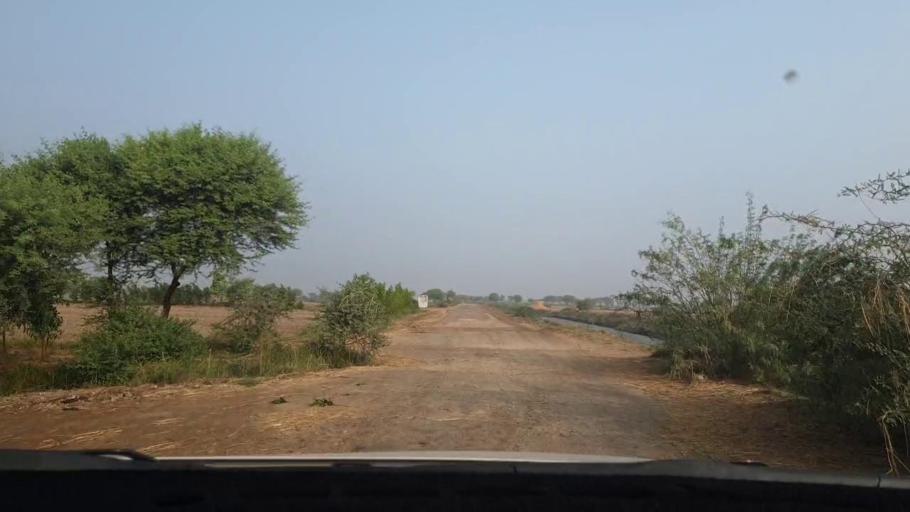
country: PK
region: Sindh
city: Tando Muhammad Khan
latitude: 25.0813
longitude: 68.4863
